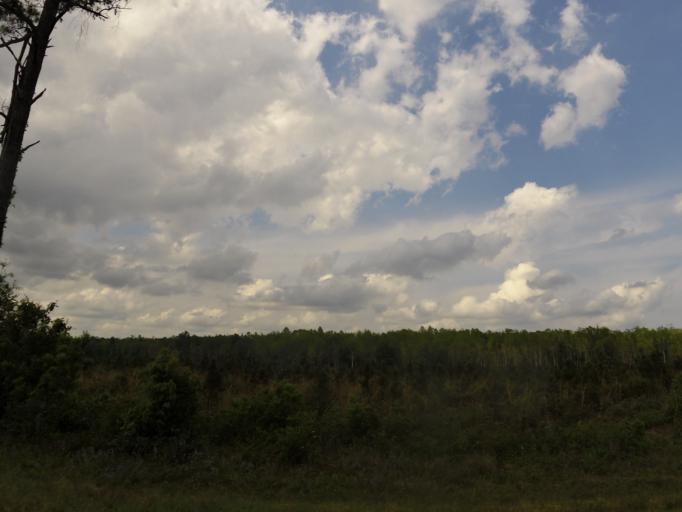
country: US
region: Georgia
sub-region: Camden County
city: Kingsland
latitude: 30.8079
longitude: -81.8253
